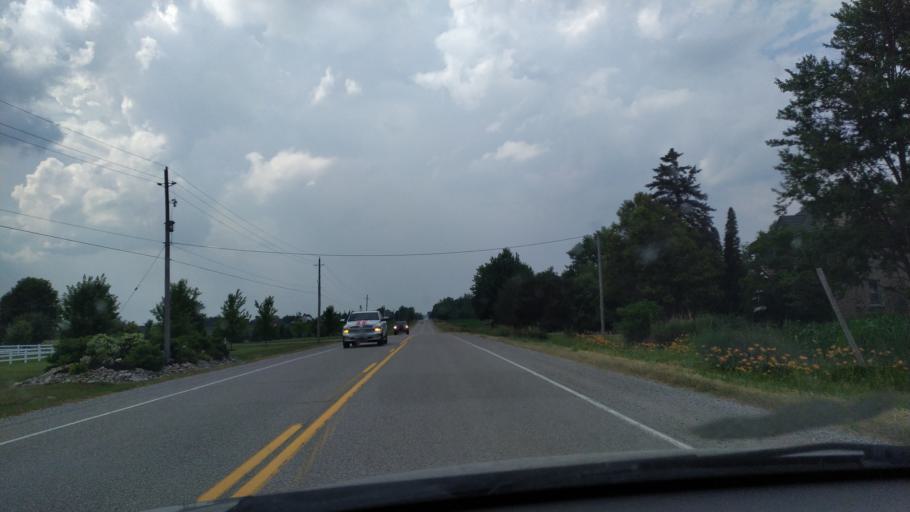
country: CA
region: Ontario
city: Dorchester
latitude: 43.1840
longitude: -81.1441
